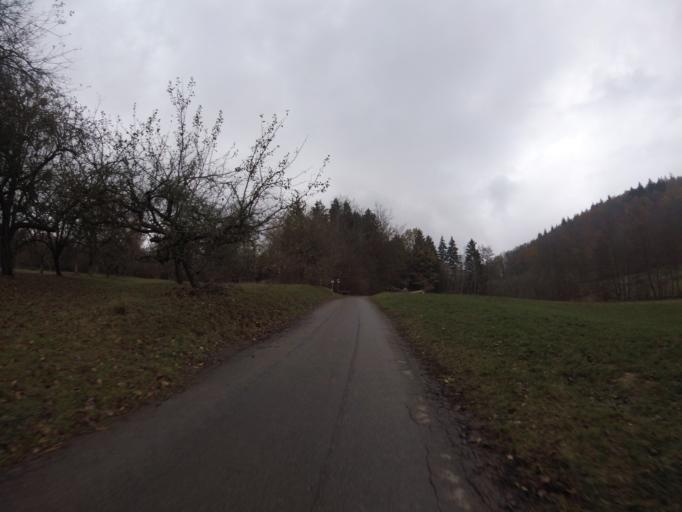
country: DE
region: Baden-Wuerttemberg
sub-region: Regierungsbezirk Stuttgart
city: Oppenweiler
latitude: 48.9810
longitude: 9.4344
